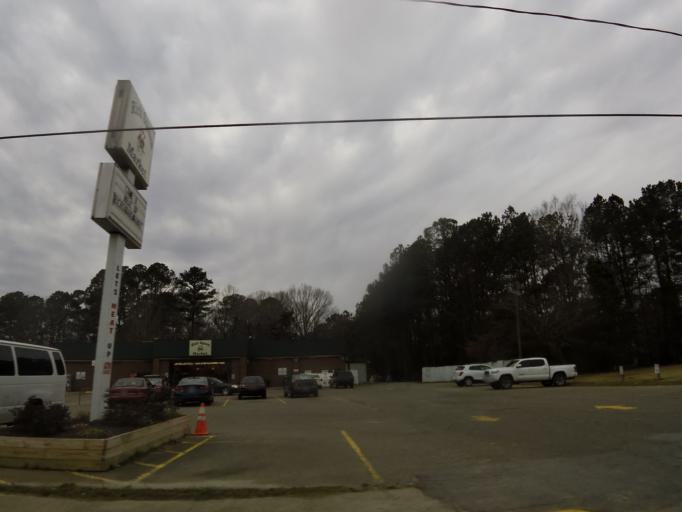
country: US
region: North Carolina
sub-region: Northampton County
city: Jackson
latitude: 36.2699
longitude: -77.2898
